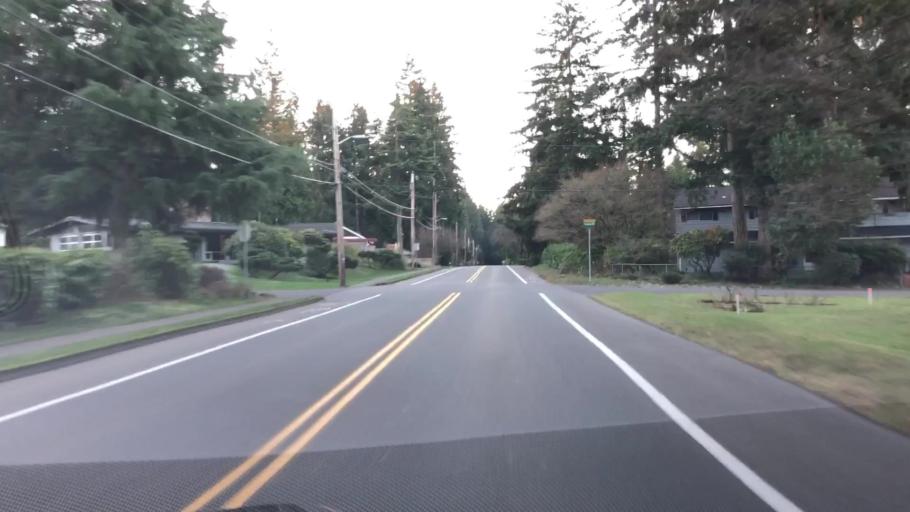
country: US
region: Washington
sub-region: King County
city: Kirkland
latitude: 47.6652
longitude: -122.1776
